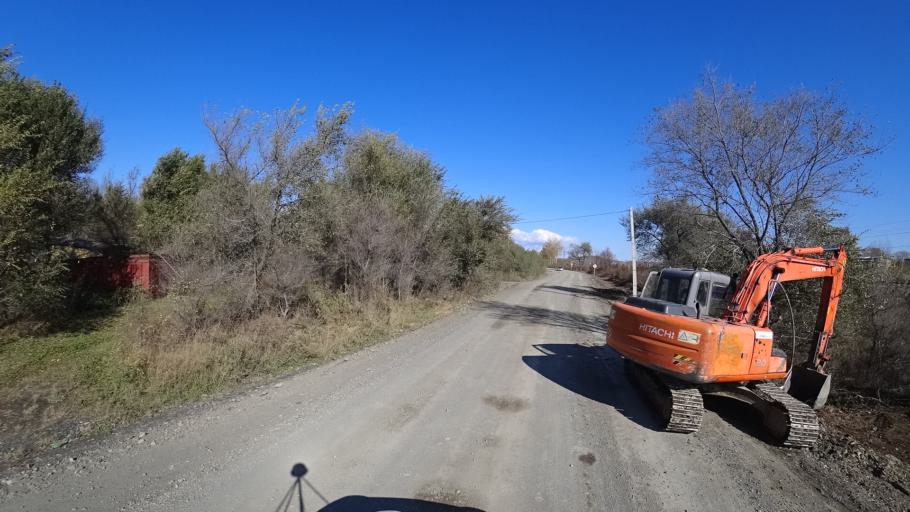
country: RU
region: Khabarovsk Krai
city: Amursk
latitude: 50.0984
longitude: 136.5053
